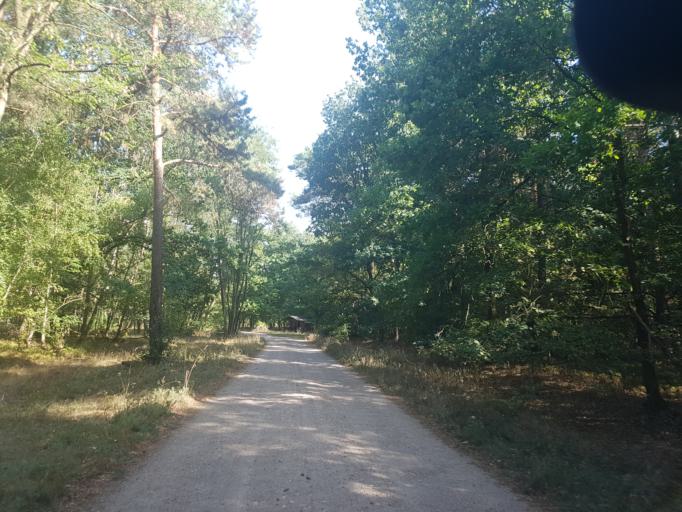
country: DE
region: Saxony-Anhalt
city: Seyda
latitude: 51.8772
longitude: 12.9549
